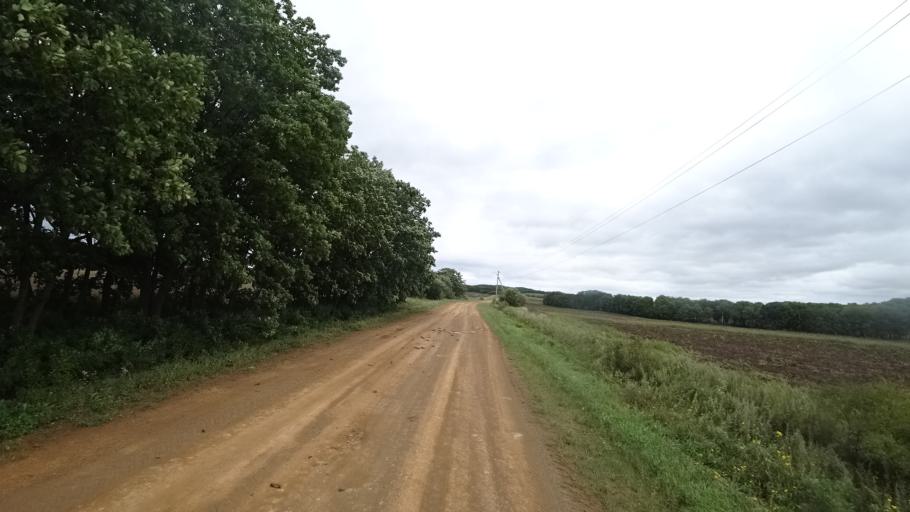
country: RU
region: Primorskiy
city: Chernigovka
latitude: 44.4442
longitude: 132.5957
